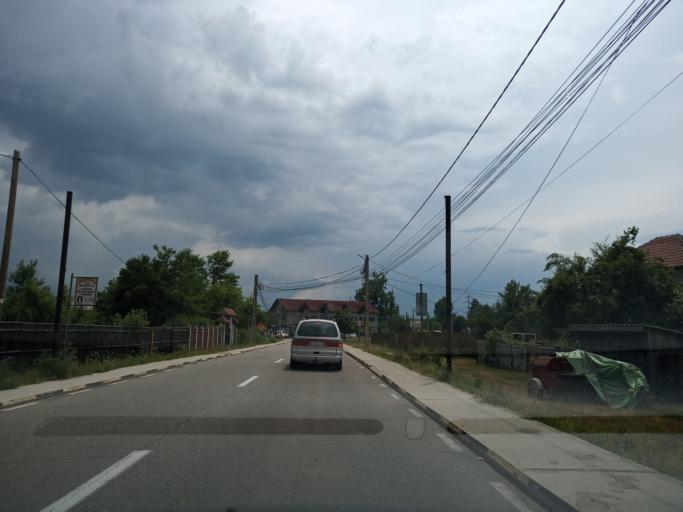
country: RO
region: Gorj
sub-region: Comuna Tismana
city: Tismana
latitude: 45.0401
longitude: 22.9520
